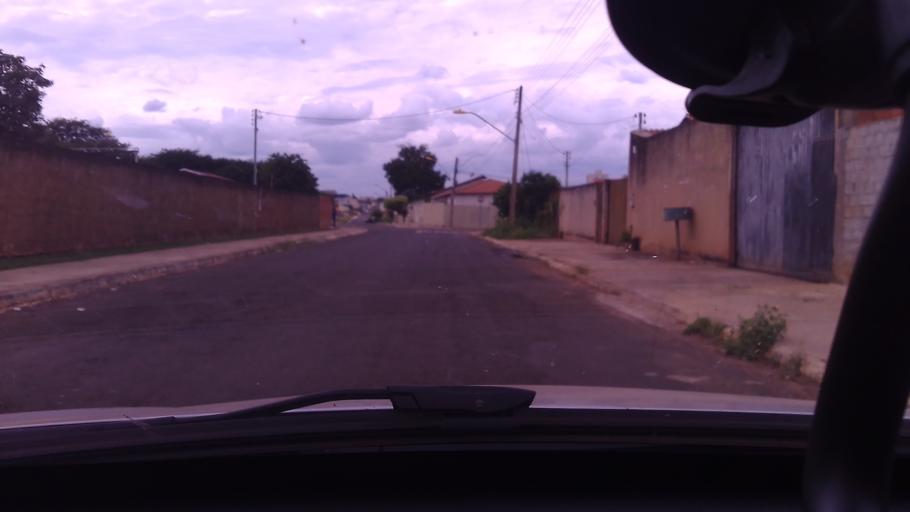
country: BR
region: Goias
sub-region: Mineiros
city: Mineiros
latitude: -17.5684
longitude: -52.5670
